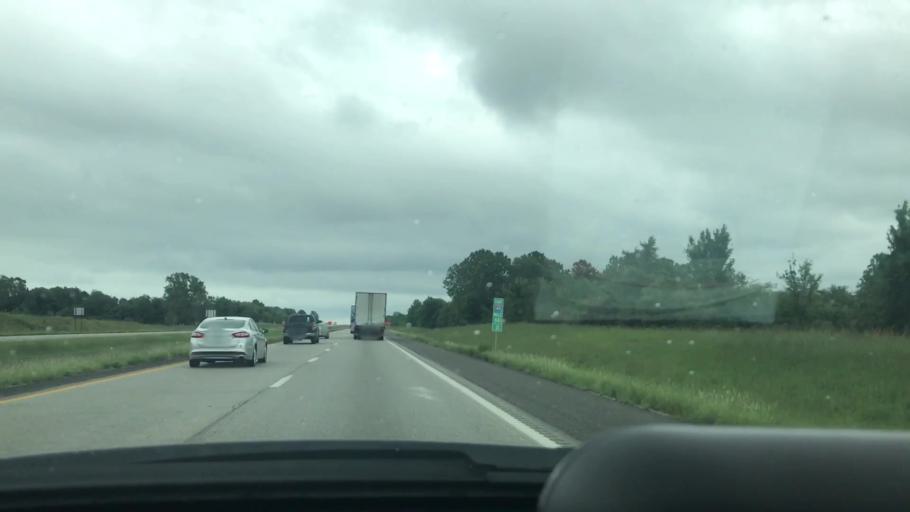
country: US
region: Missouri
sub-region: Greene County
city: Ash Grove
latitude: 37.1866
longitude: -93.6053
